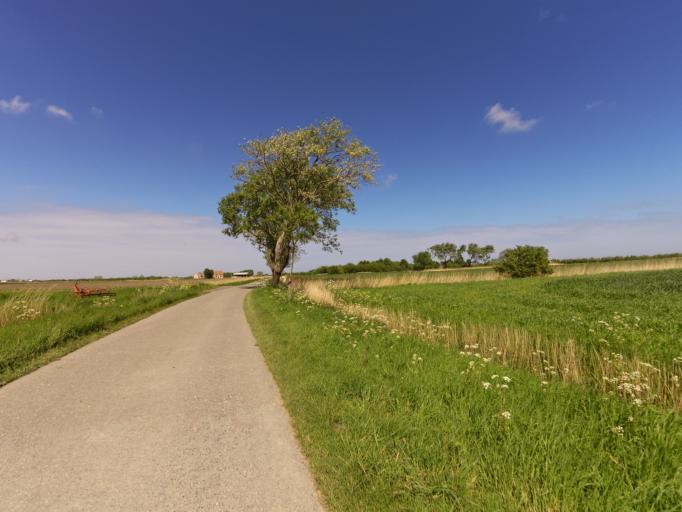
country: BE
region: Flanders
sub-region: Provincie West-Vlaanderen
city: Middelkerke
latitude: 51.1346
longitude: 2.8458
